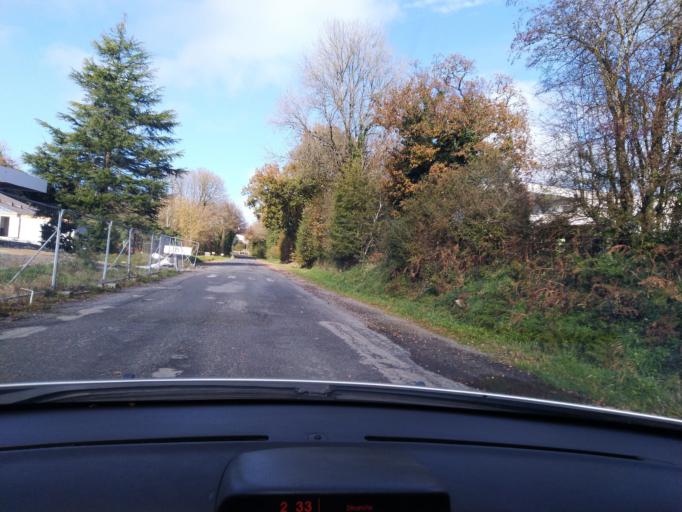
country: FR
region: Brittany
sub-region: Departement du Finistere
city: Guerlesquin
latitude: 48.5126
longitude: -3.5915
